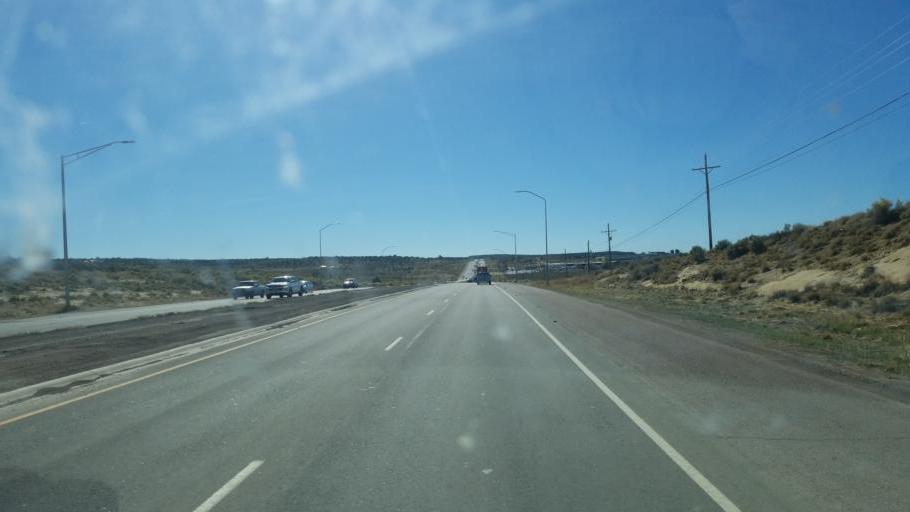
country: US
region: New Mexico
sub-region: McKinley County
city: Twin Lakes
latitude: 35.6163
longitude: -108.7789
